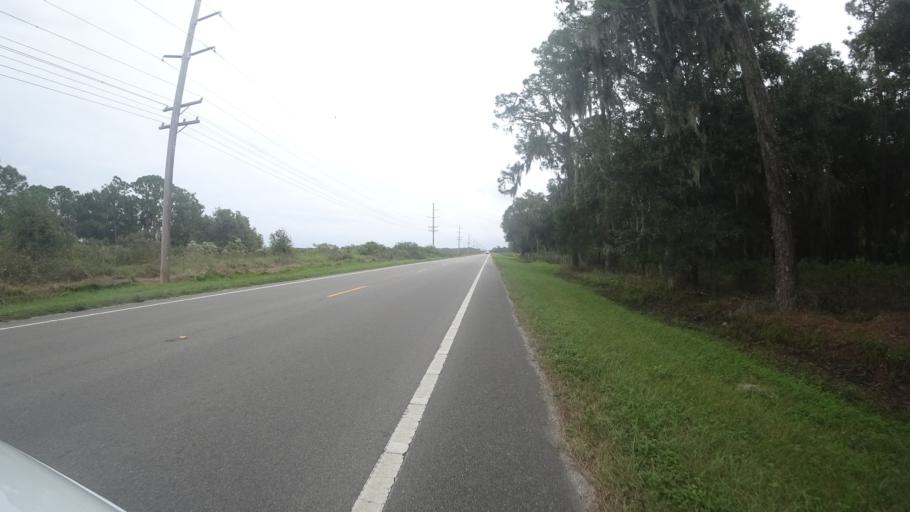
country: US
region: Florida
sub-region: Hillsborough County
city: Wimauma
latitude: 27.5894
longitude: -82.1418
